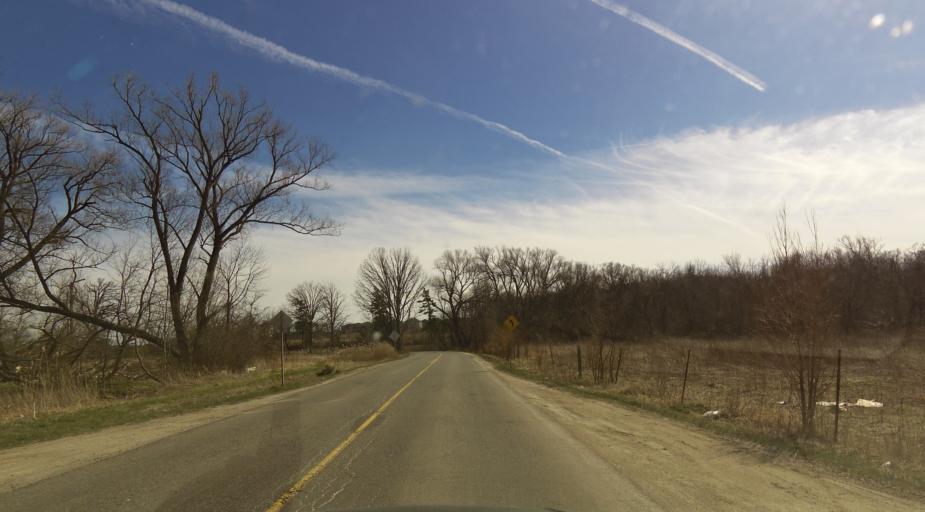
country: CA
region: Ontario
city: Brampton
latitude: 43.6421
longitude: -79.7707
